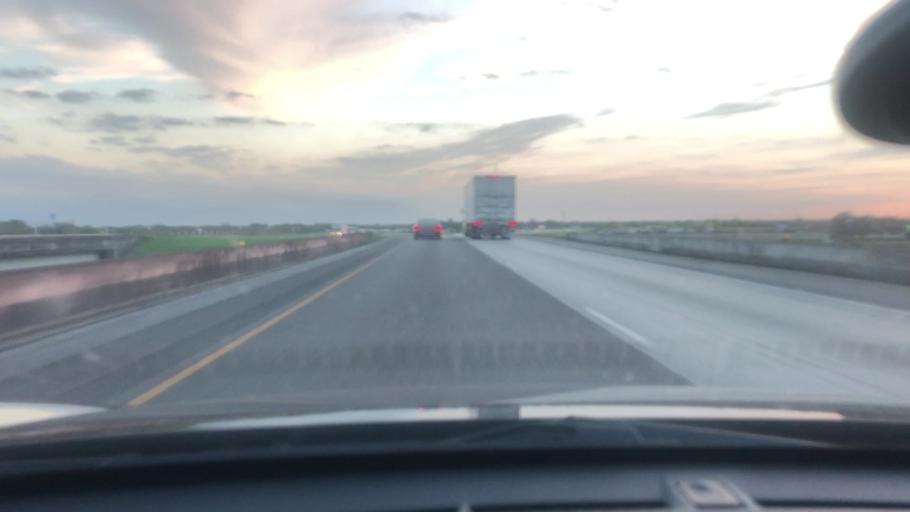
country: US
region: Texas
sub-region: Jackson County
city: Edna
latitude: 28.9695
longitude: -96.6708
